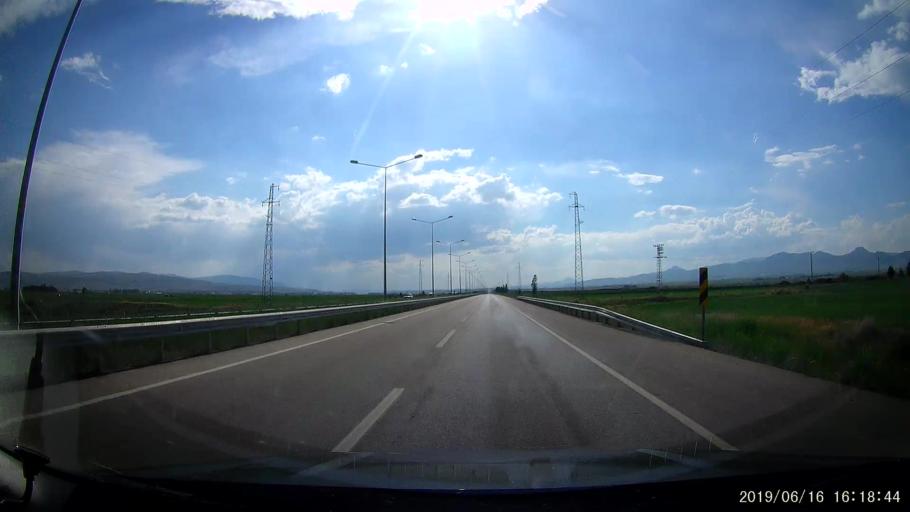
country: TR
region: Erzurum
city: Ilica
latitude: 39.9653
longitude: 41.1601
